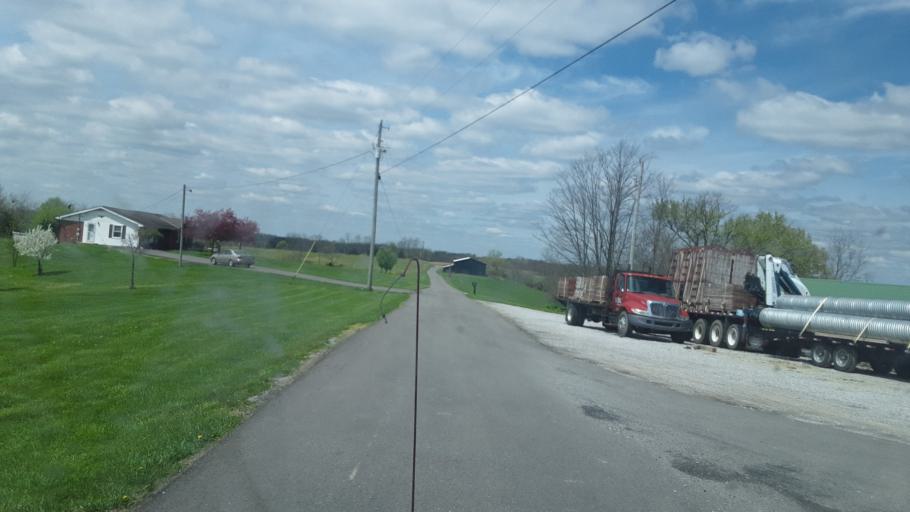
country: US
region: Kentucky
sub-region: Owen County
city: Owenton
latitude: 38.6729
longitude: -84.7844
